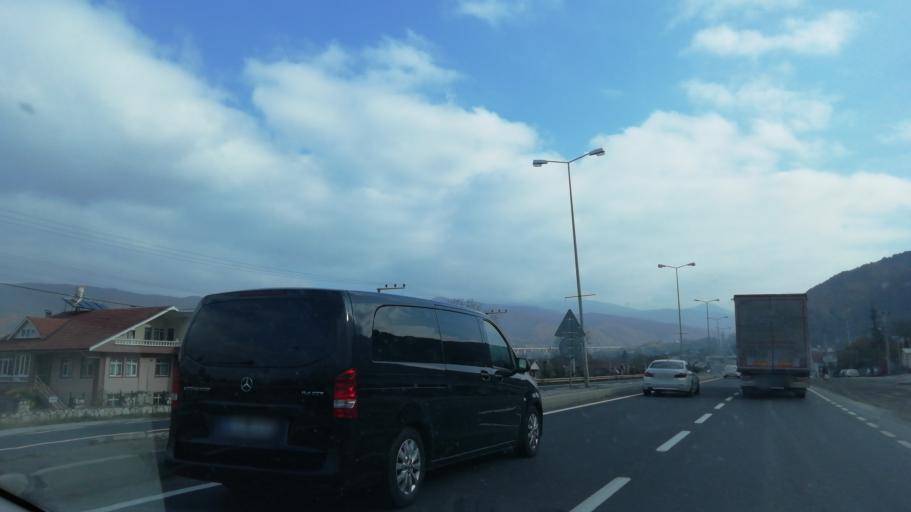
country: TR
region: Duzce
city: Kaynasli
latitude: 40.7731
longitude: 31.3223
